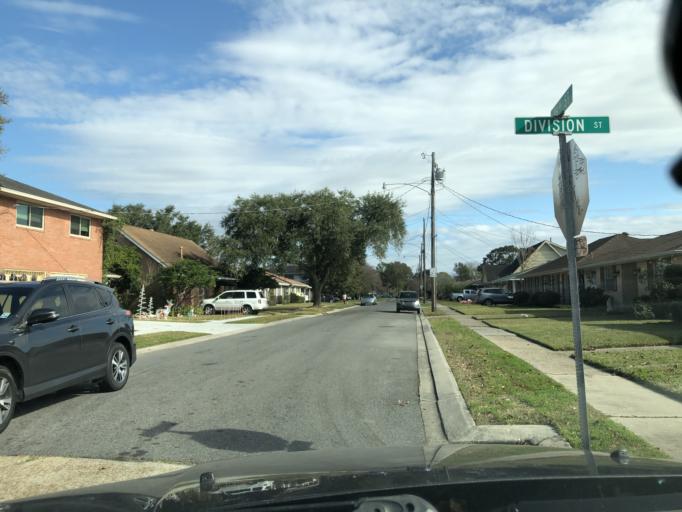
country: US
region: Louisiana
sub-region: Jefferson Parish
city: Metairie Terrace
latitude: 29.9855
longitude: -90.1645
